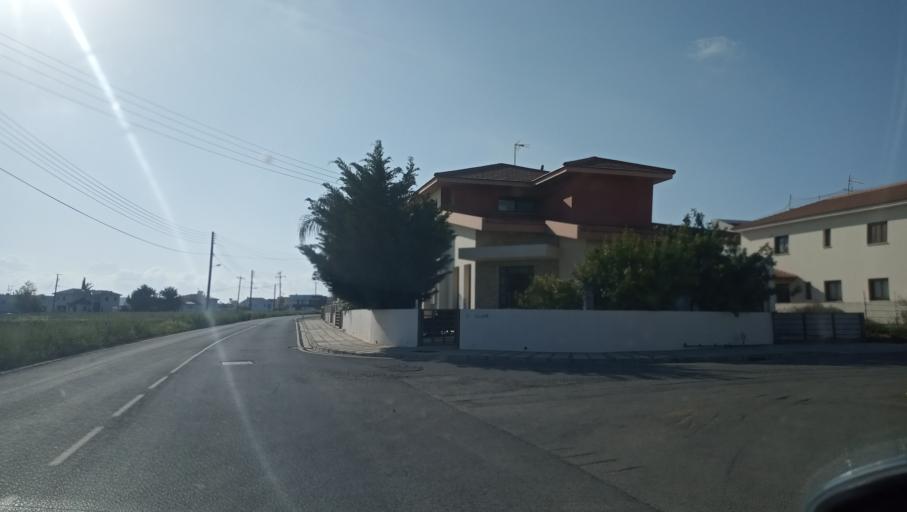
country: CY
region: Lefkosia
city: Tseri
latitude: 35.0816
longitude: 33.3161
